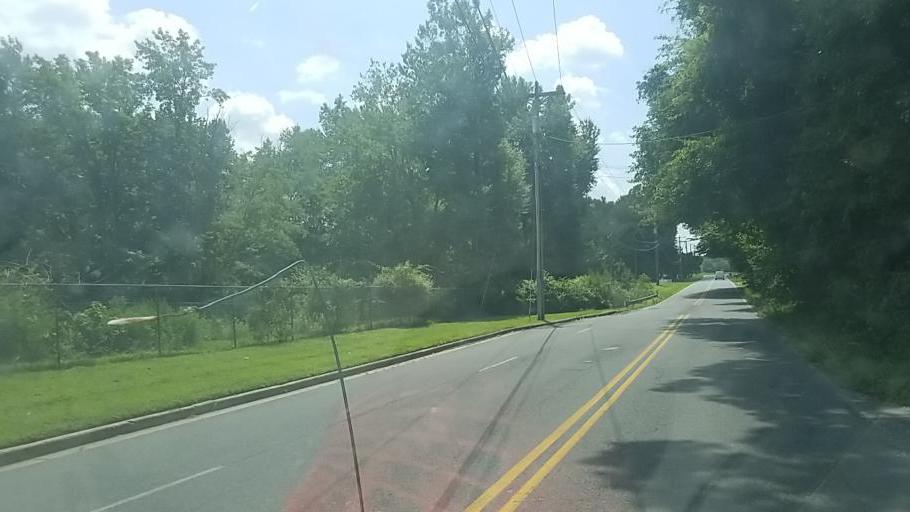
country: US
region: Maryland
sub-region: Wicomico County
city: Salisbury
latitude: 38.3629
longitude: -75.5480
